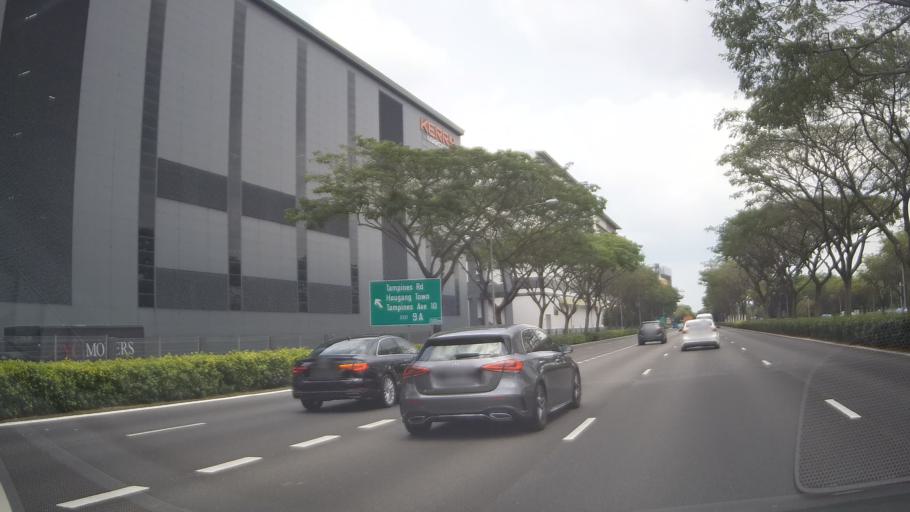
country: SG
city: Singapore
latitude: 1.3696
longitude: 103.9078
